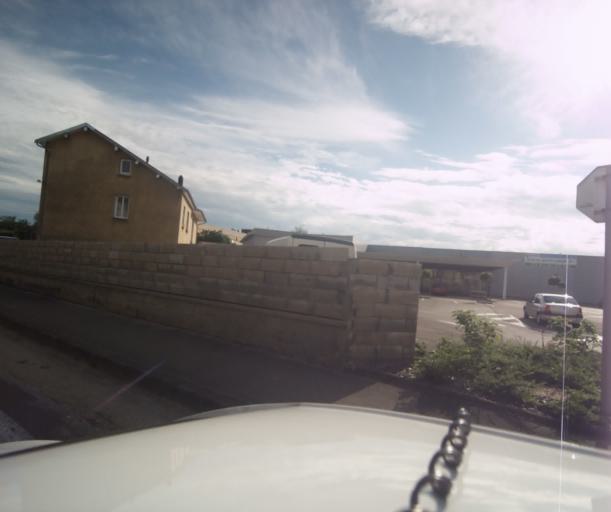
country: FR
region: Franche-Comte
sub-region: Departement du Doubs
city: Besancon
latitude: 47.2368
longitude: 5.9886
